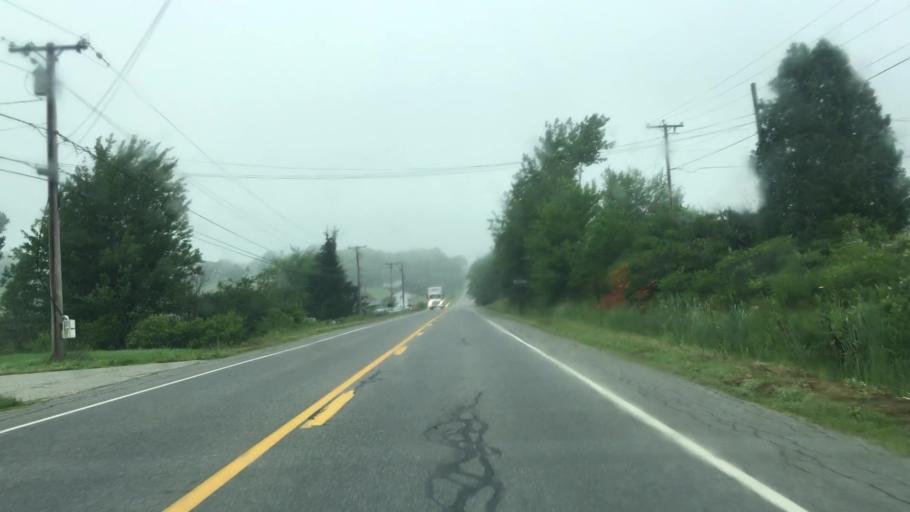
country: US
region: Maine
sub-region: Lincoln County
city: Wiscasset
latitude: 44.0394
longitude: -69.6738
